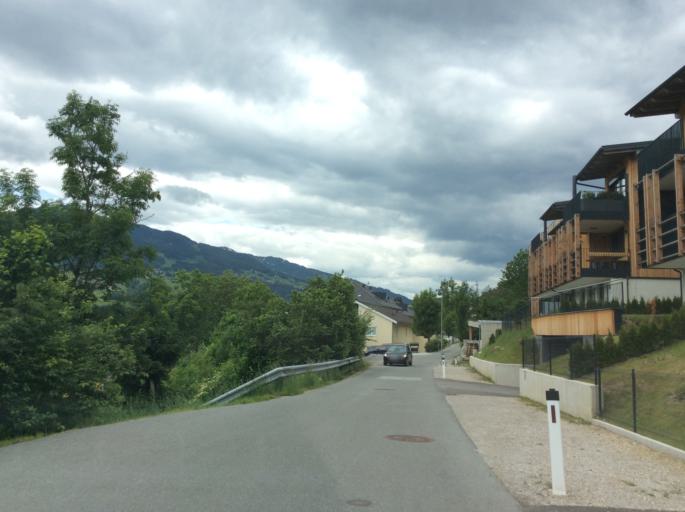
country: AT
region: Styria
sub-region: Politischer Bezirk Liezen
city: Schladming
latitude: 47.3999
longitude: 13.6932
